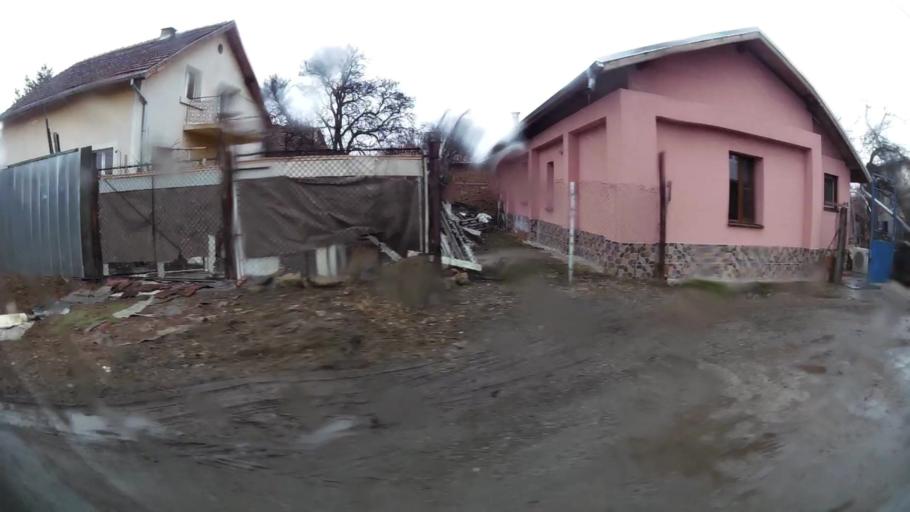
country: BG
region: Sofia-Capital
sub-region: Stolichna Obshtina
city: Sofia
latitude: 42.6632
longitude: 23.4280
